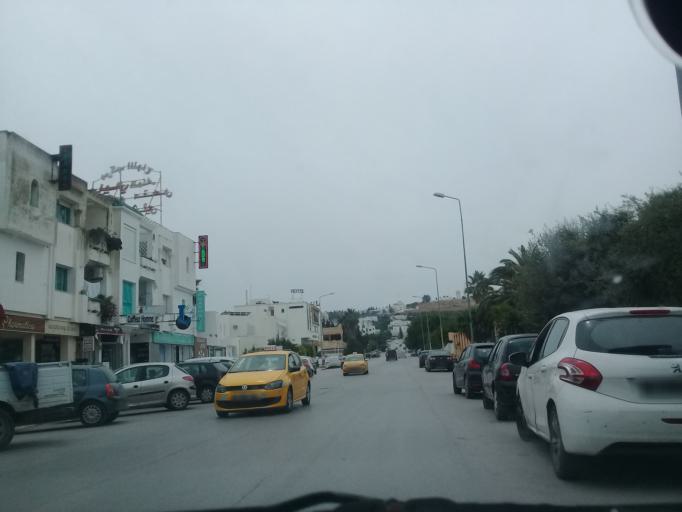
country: TN
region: Tunis
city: Tunis
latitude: 36.8422
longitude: 10.1579
